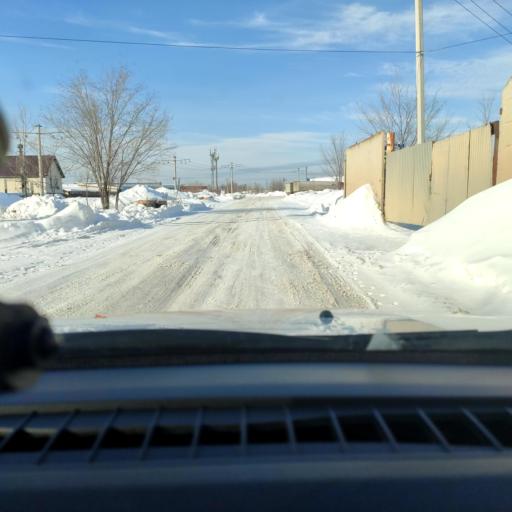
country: RU
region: Samara
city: Petra-Dubrava
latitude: 53.2619
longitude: 50.3548
